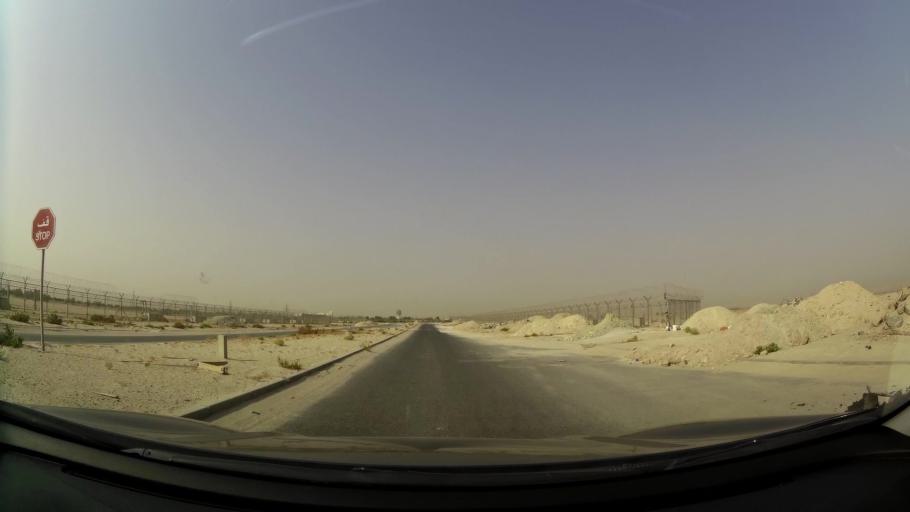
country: KW
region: Muhafazat al Jahra'
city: Al Jahra'
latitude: 29.3449
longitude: 47.7286
